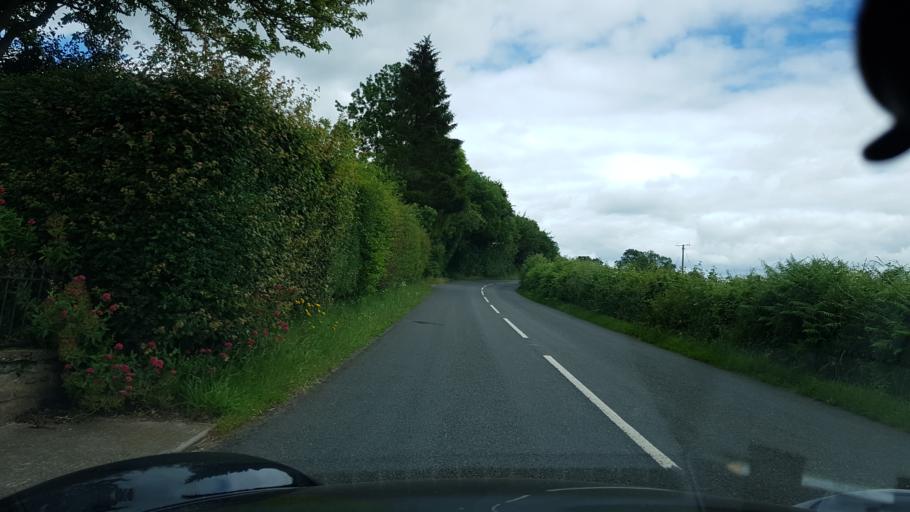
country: GB
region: Wales
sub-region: Monmouthshire
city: Grosmont
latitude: 51.8589
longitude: -2.8965
